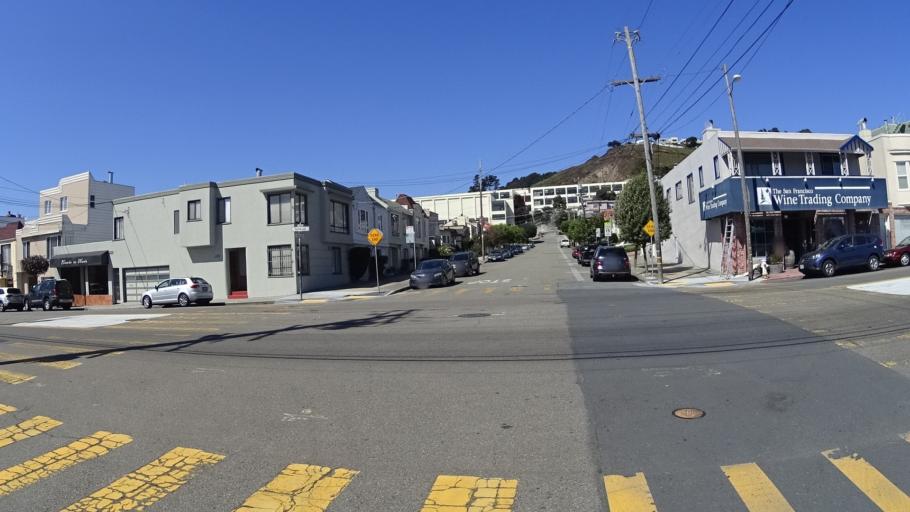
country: US
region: California
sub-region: San Mateo County
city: Daly City
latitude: 37.7432
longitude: -122.4692
